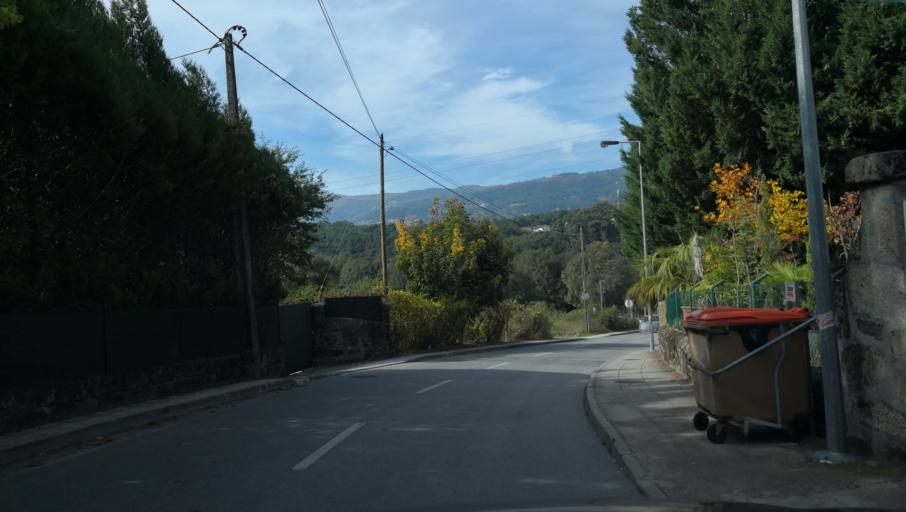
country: PT
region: Vila Real
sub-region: Vila Real
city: Vila Real
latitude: 41.3175
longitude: -7.7409
